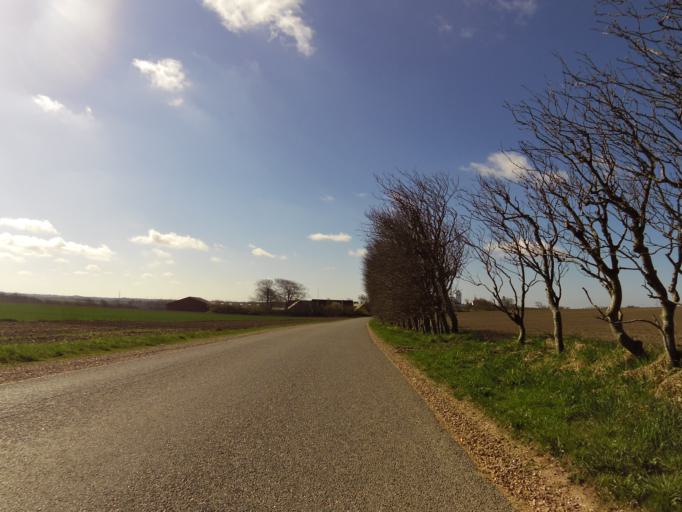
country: DK
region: Central Jutland
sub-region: Holstebro Kommune
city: Vinderup
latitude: 56.4524
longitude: 8.7238
